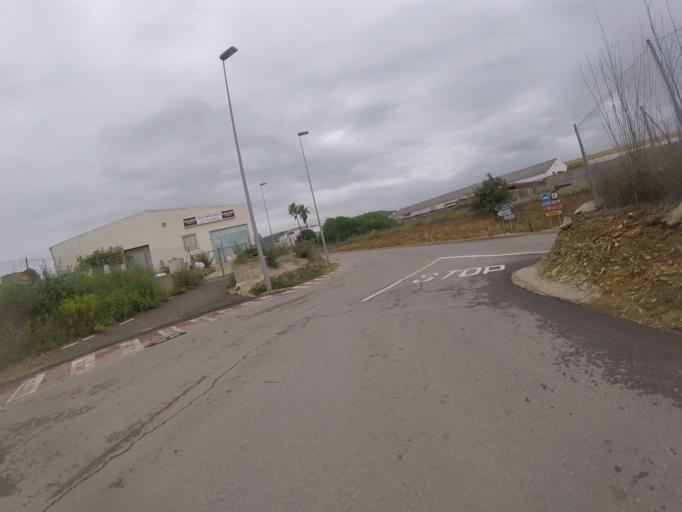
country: ES
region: Valencia
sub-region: Provincia de Castello
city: Alcala de Xivert
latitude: 40.3080
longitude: 0.2296
